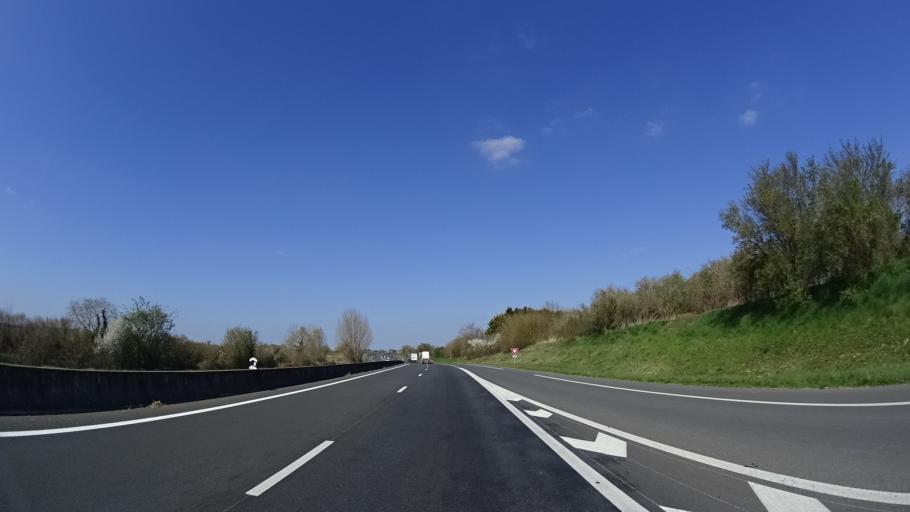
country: FR
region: Pays de la Loire
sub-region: Departement de Maine-et-Loire
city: Saint-Jean
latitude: 47.2459
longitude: -0.3227
